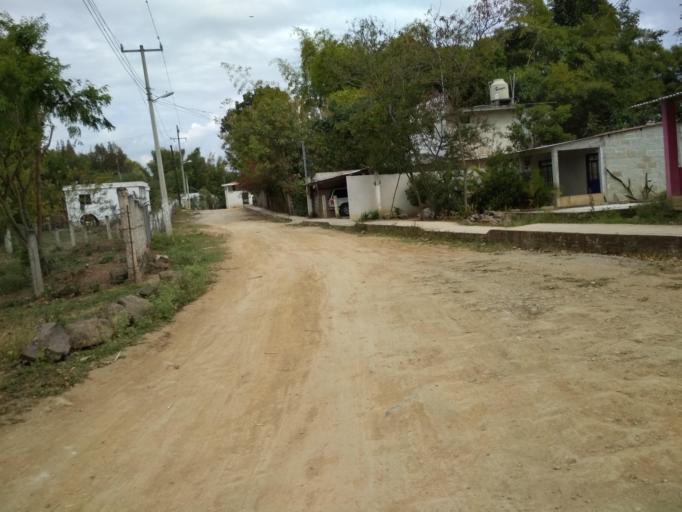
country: MX
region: Veracruz
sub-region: Coatepec
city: Tuzamapan
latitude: 19.3681
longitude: -96.8797
